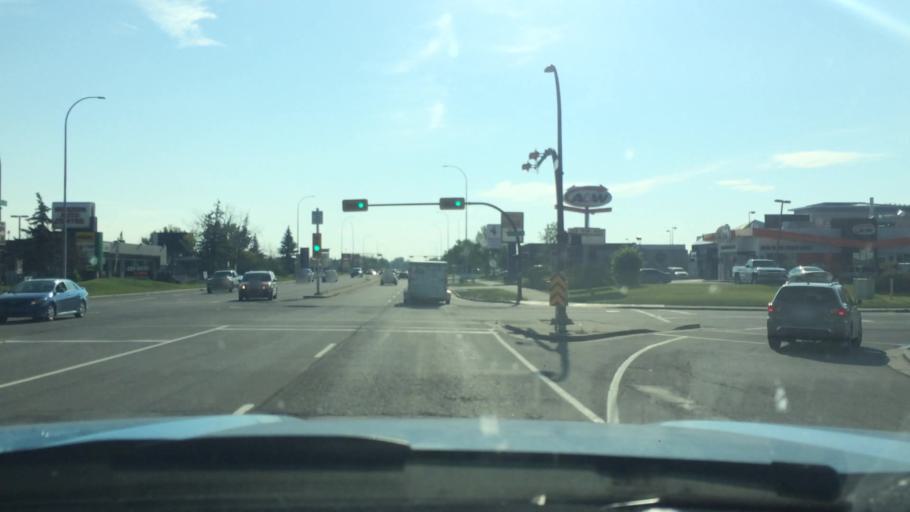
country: CA
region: Alberta
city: Calgary
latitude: 51.0814
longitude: -113.9892
